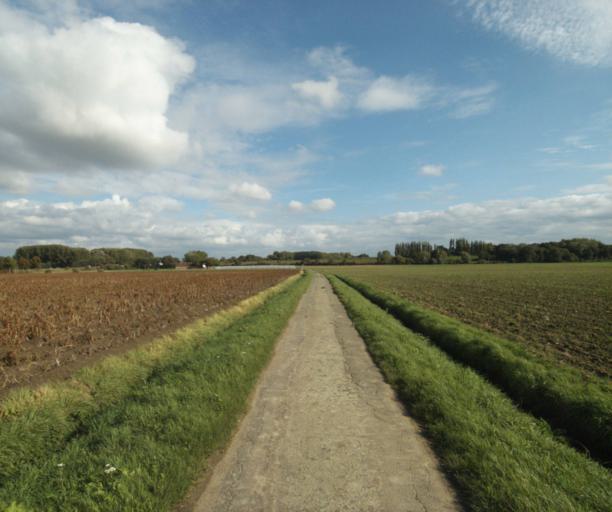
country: FR
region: Nord-Pas-de-Calais
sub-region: Departement du Nord
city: Ennetieres-en-Weppes
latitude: 50.6434
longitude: 2.9242
